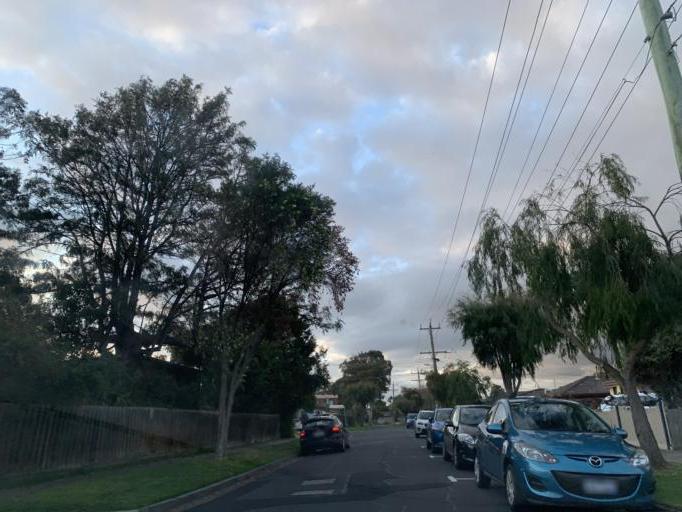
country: AU
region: Victoria
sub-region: Kingston
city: Aspendale
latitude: -38.0175
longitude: 145.1016
